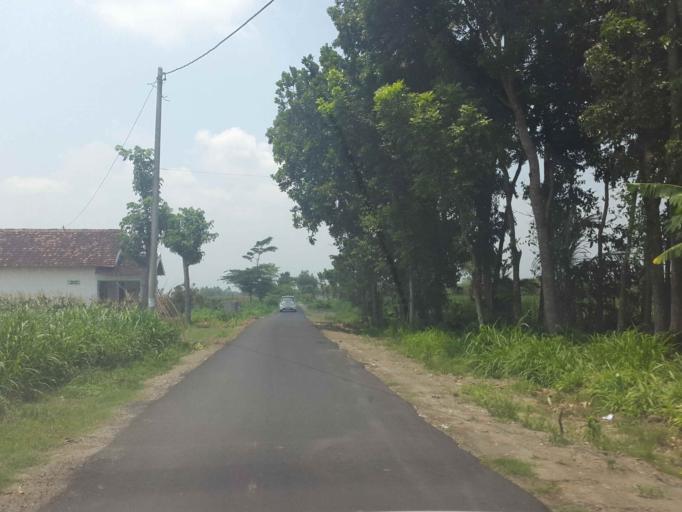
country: ID
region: East Java
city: Temenggungan
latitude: -7.9395
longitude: 112.0852
